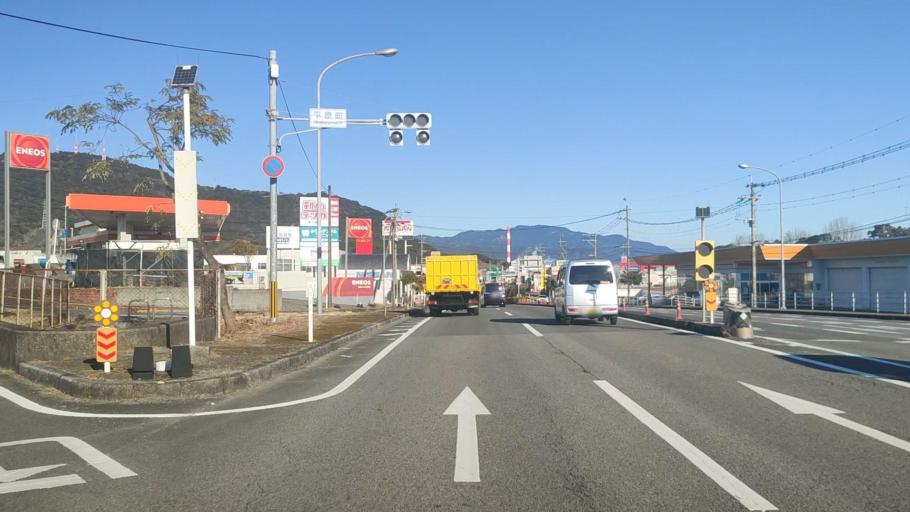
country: JP
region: Miyazaki
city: Nobeoka
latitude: 32.5451
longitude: 131.6778
